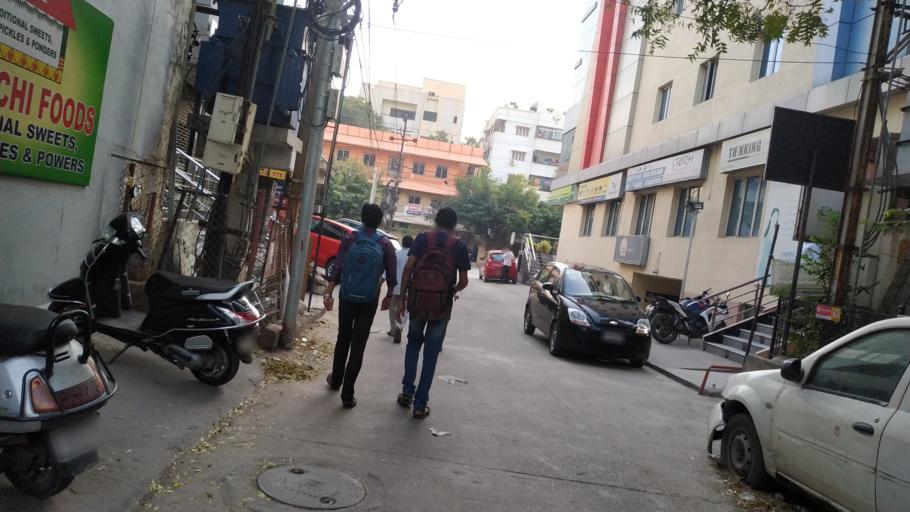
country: IN
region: Telangana
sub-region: Rangareddi
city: Kukatpalli
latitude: 17.4422
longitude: 78.4467
